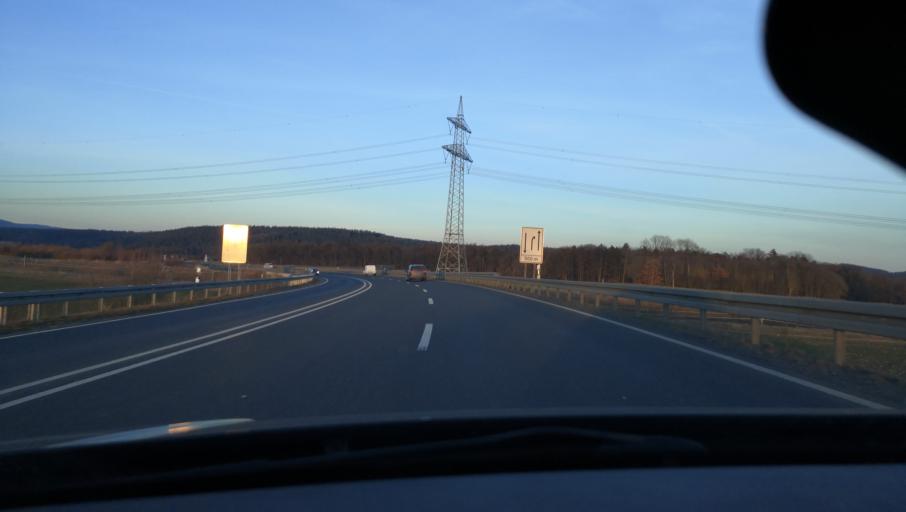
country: DE
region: Bavaria
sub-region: Upper Franconia
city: Rodental
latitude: 50.2976
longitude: 11.0076
